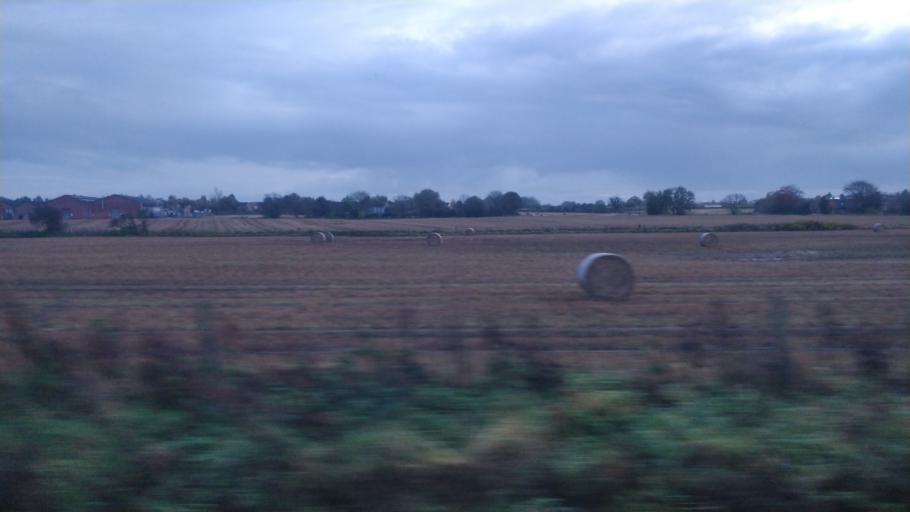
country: GB
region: England
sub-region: Lancashire
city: Ormskirk
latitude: 53.6073
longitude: -2.8505
